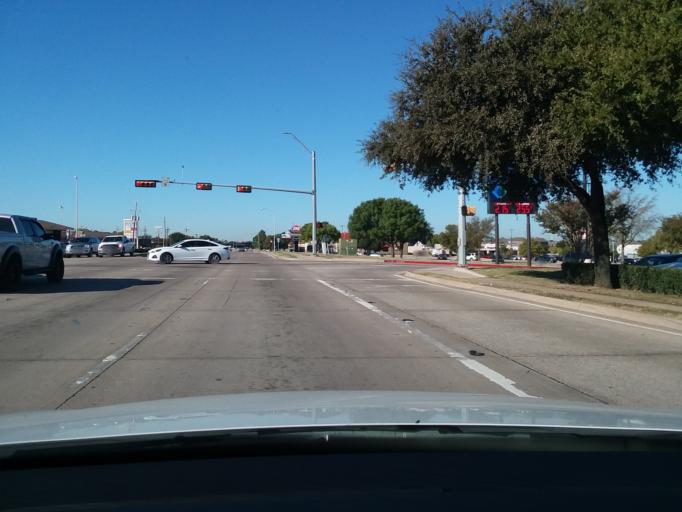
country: US
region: Texas
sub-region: Denton County
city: Lewisville
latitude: 33.0462
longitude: -97.0113
